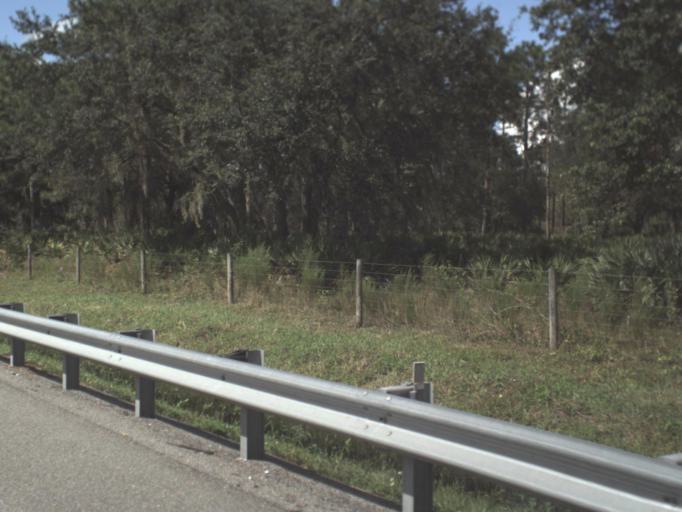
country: US
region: Florida
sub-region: Sarasota County
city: Lake Sarasota
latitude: 27.3773
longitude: -82.2299
